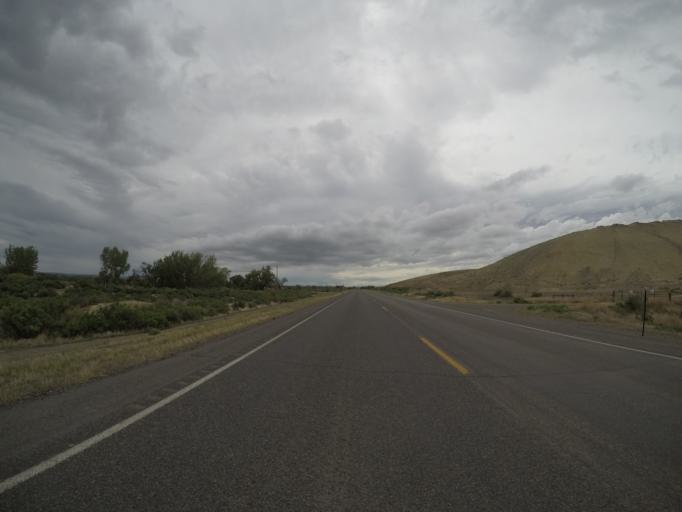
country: US
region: Wyoming
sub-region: Big Horn County
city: Lovell
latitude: 44.8743
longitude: -108.3109
